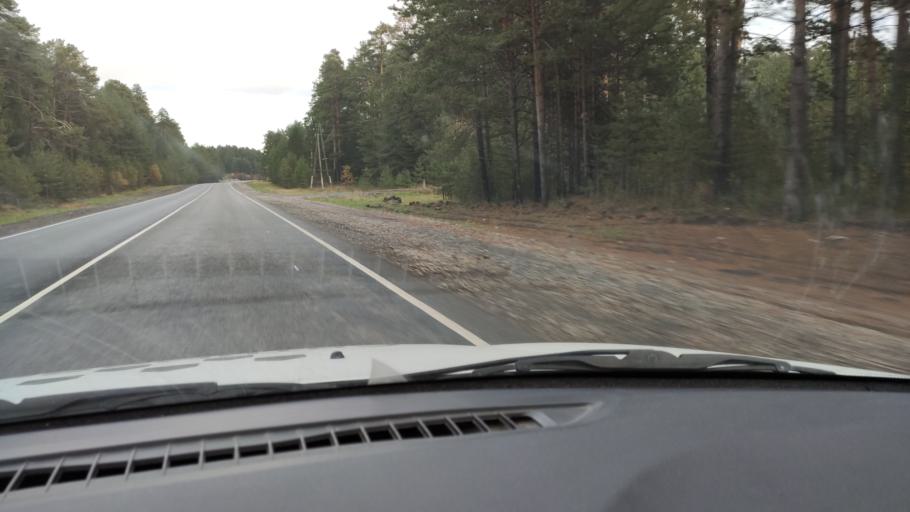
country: RU
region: Kirov
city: Belaya Kholunitsa
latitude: 58.8557
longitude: 50.8391
